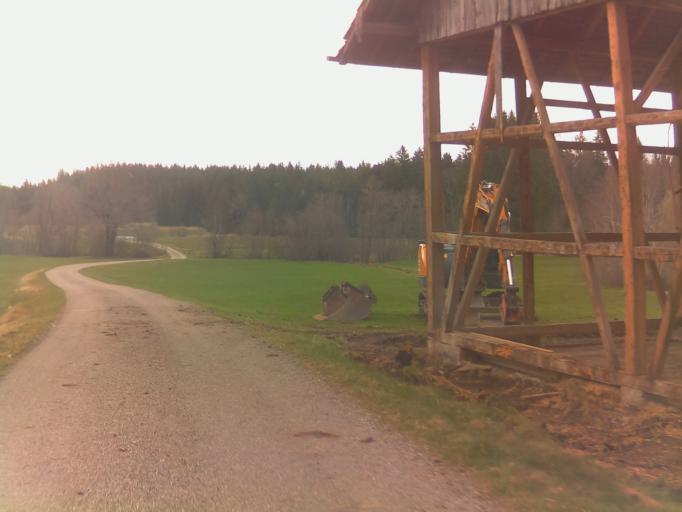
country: DE
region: Bavaria
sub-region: Upper Bavaria
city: Bobing
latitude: 47.7331
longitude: 11.0458
